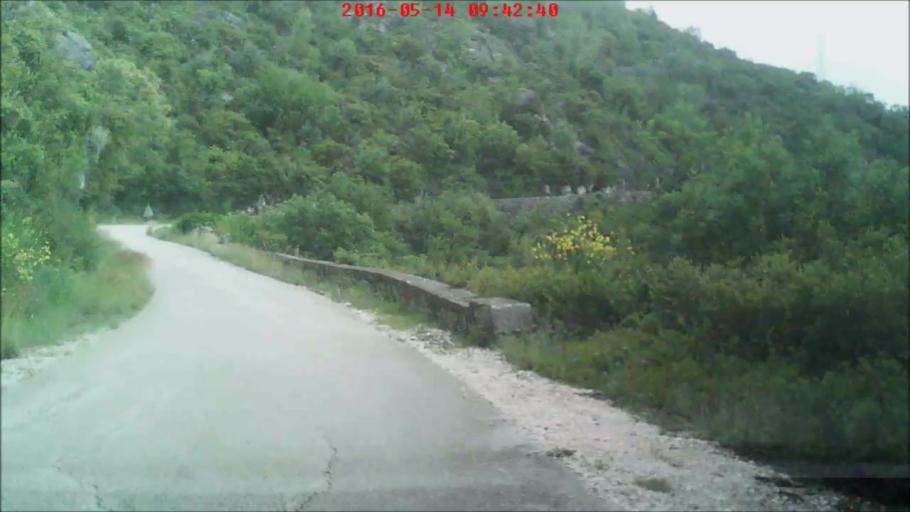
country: HR
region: Dubrovacko-Neretvanska
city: Podgora
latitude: 42.7885
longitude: 17.9032
